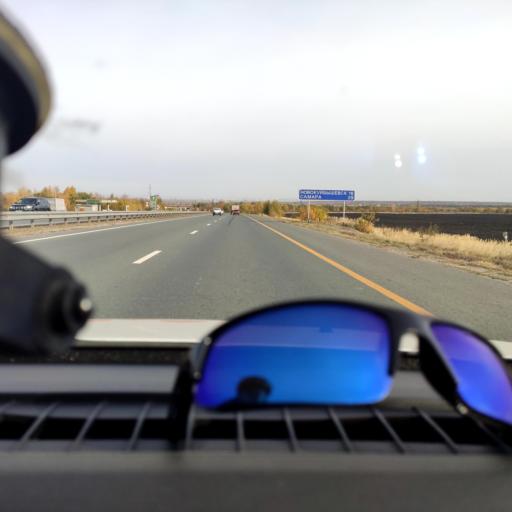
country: RU
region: Samara
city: Novokuybyshevsk
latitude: 53.0145
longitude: 49.9801
